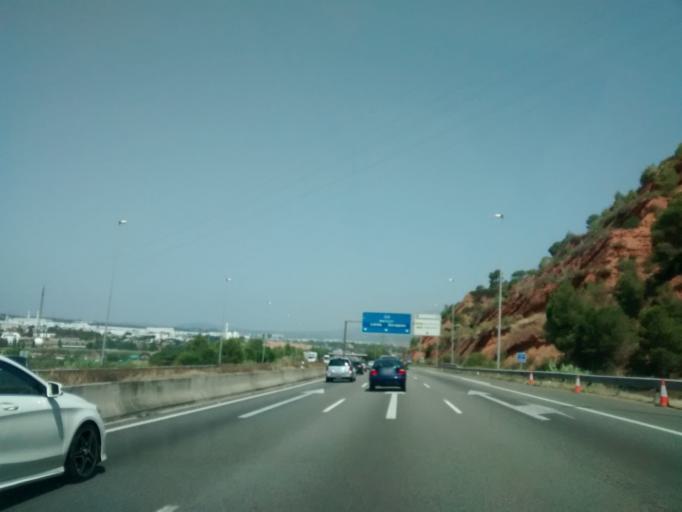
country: ES
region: Catalonia
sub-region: Provincia de Barcelona
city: Martorell
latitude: 41.4877
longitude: 1.9321
